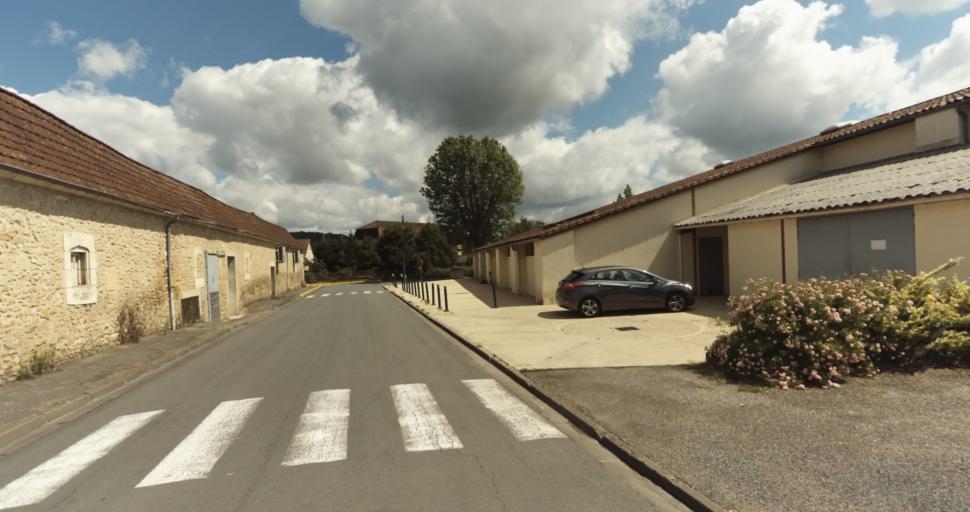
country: FR
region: Aquitaine
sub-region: Departement de la Dordogne
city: Le Bugue
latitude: 44.8454
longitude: 0.9120
